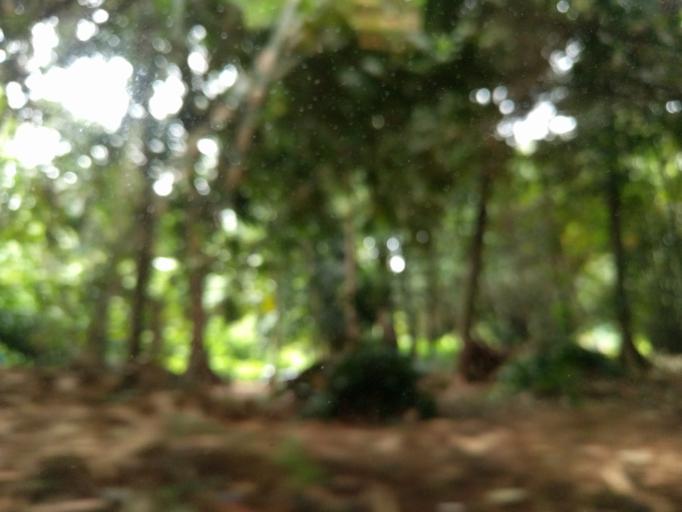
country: ID
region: West Java
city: Bogor
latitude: -6.5996
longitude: 106.7957
